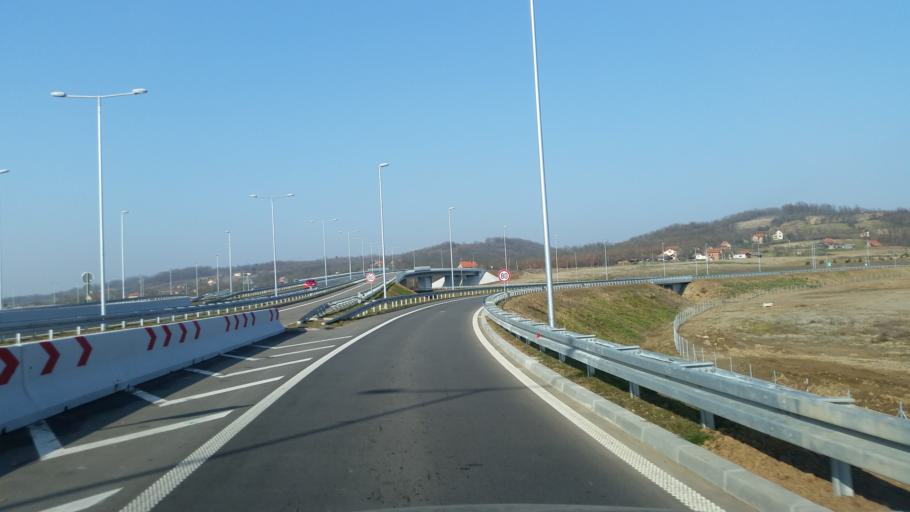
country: RS
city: Prislonica
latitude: 43.9182
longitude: 20.3959
